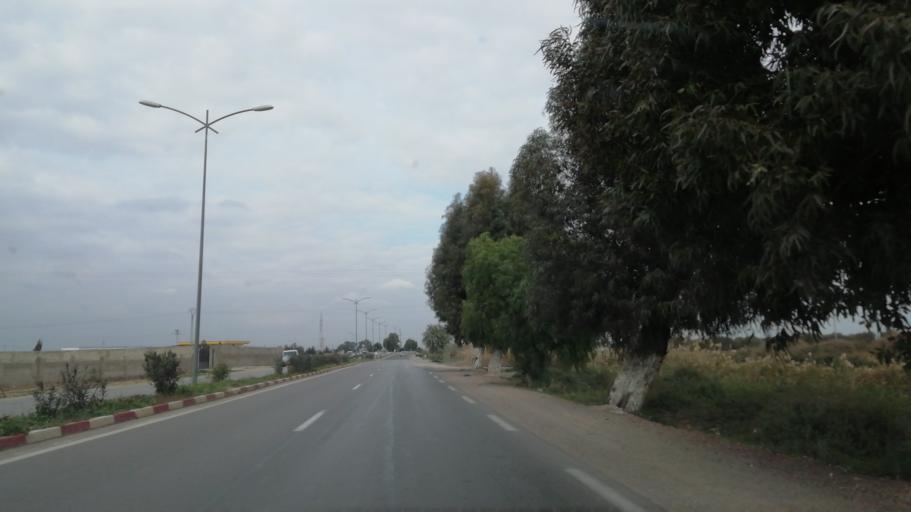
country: DZ
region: Mascara
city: Mascara
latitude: 35.6261
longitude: 0.0617
